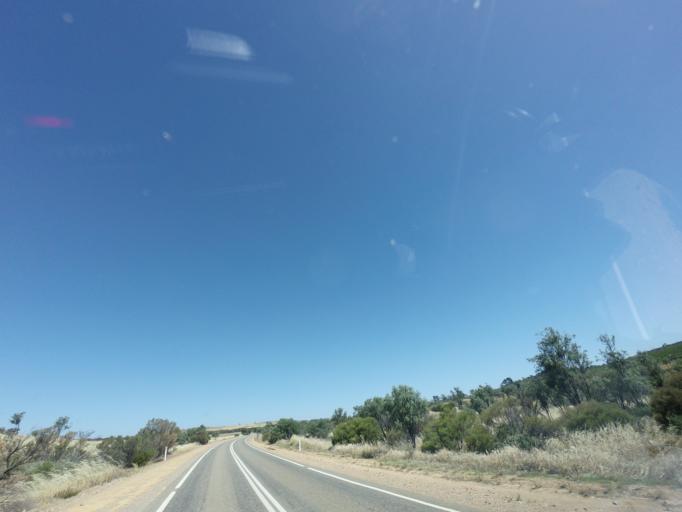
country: AU
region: South Australia
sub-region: Peterborough
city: Peterborough
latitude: -32.9146
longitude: 138.7670
